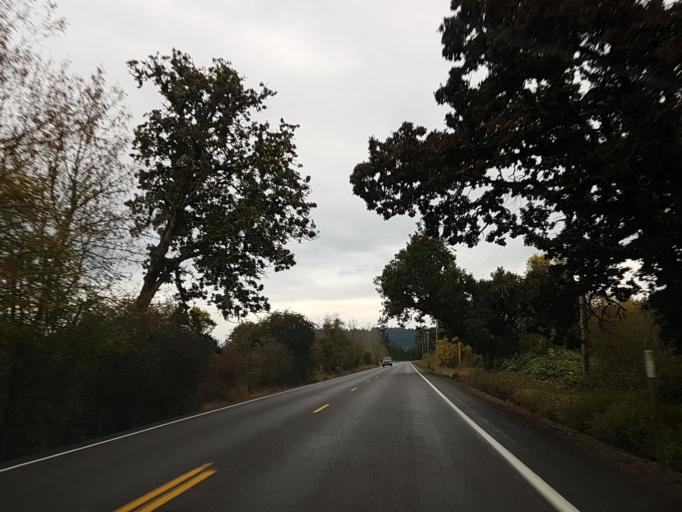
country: US
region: Oregon
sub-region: Marion County
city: Stayton
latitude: 44.7099
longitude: -122.7908
